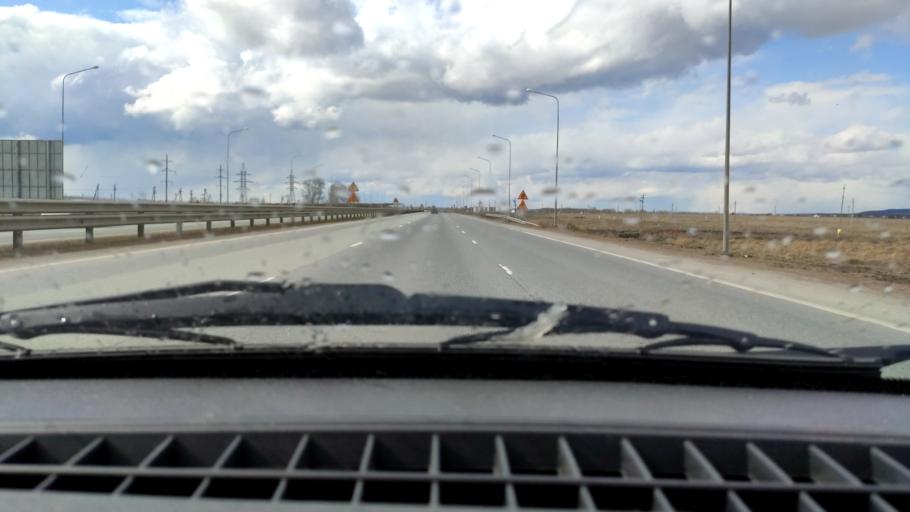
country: RU
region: Bashkortostan
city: Asanovo
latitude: 54.8973
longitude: 55.6367
